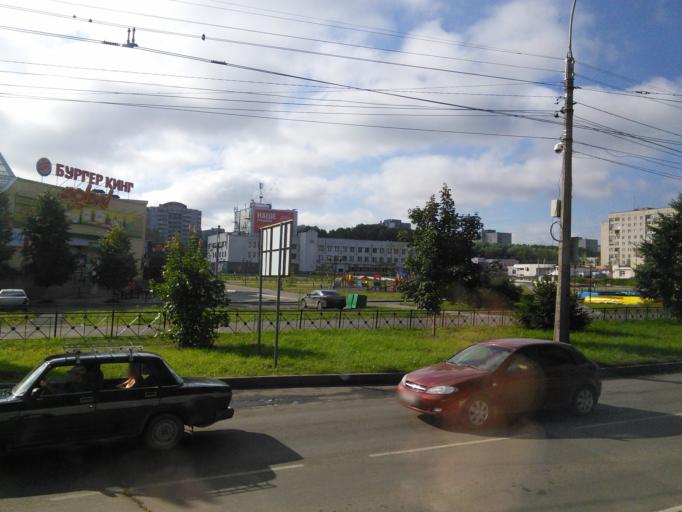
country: RU
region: Vologda
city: Vologda
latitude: 59.2056
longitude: 39.8378
